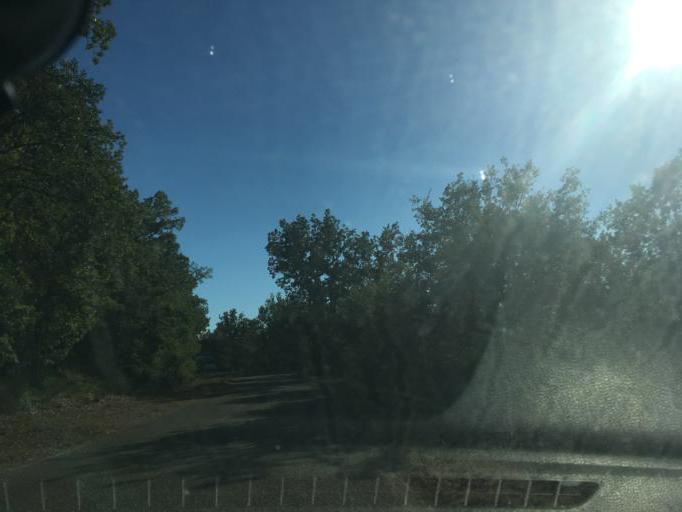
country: FR
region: Provence-Alpes-Cote d'Azur
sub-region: Departement du Var
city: Regusse
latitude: 43.6910
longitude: 6.1541
